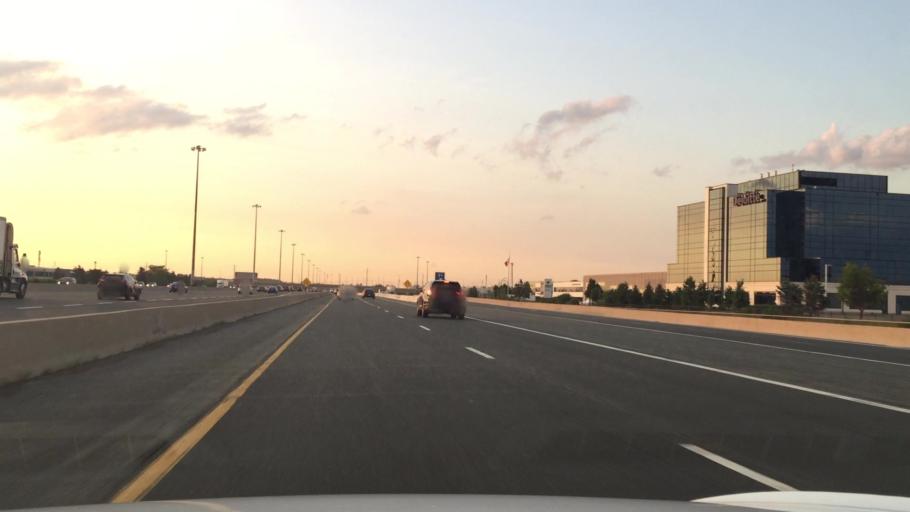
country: CA
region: Ontario
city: Vaughan
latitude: 43.8023
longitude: -79.5416
